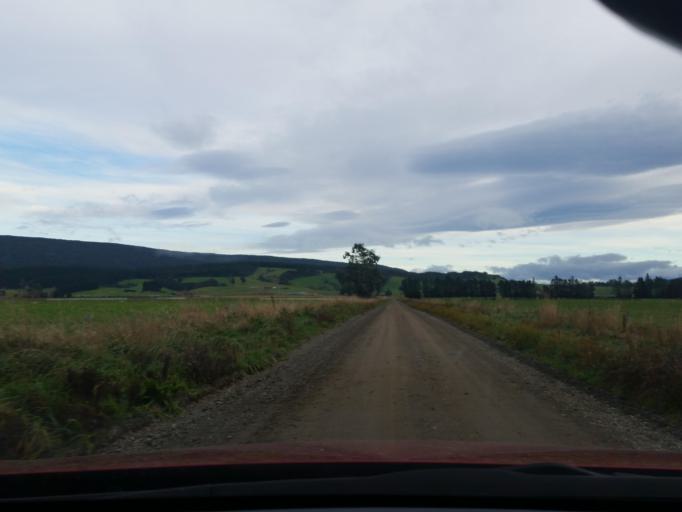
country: NZ
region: Southland
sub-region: Southland District
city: Riverton
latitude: -46.0997
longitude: 167.9608
